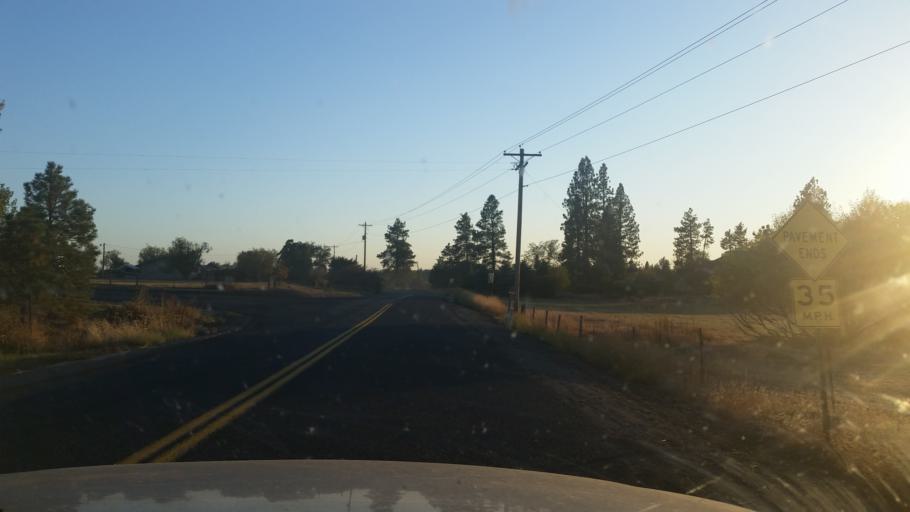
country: US
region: Washington
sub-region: Spokane County
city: Medical Lake
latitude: 47.5396
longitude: -117.6340
